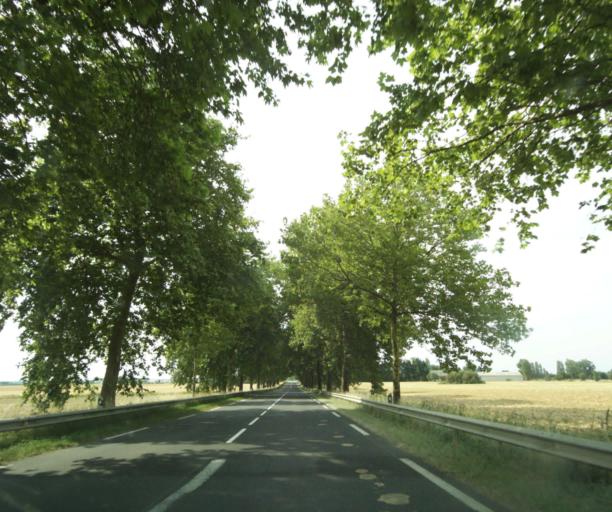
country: FR
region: Centre
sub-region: Departement d'Indre-et-Loire
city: Neuille-Pont-Pierre
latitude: 47.5928
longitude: 0.5324
